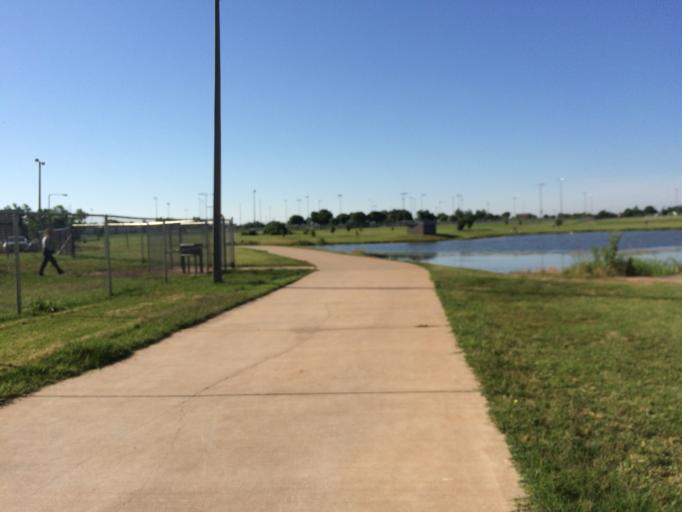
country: US
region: Oklahoma
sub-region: Cleveland County
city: Norman
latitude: 35.2380
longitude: -97.4276
